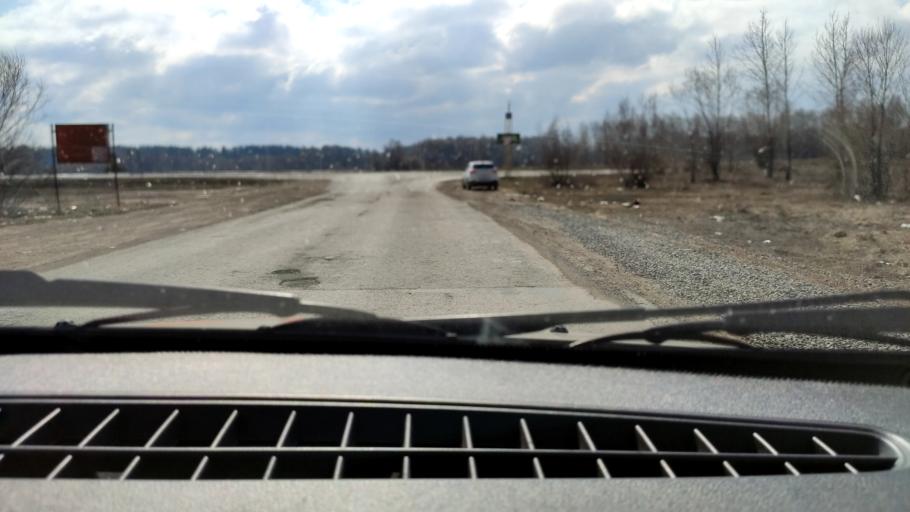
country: RU
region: Bashkortostan
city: Kudeyevskiy
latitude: 54.8183
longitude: 56.7937
